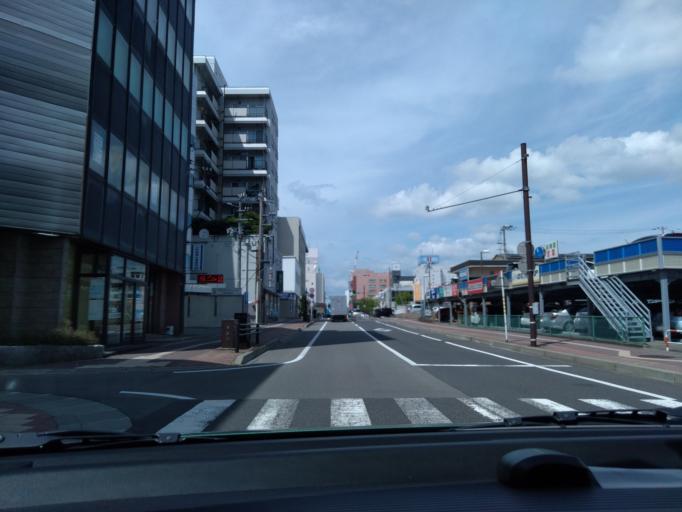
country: JP
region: Akita
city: Akita
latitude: 39.7131
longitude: 140.1249
